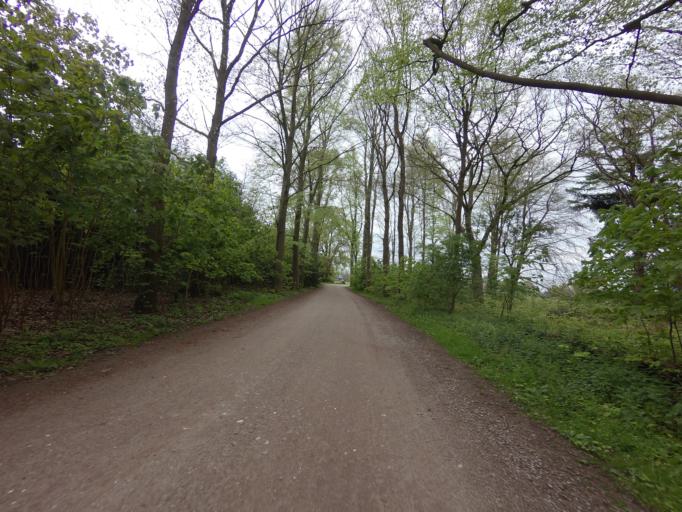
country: NL
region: Utrecht
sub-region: Gemeente De Bilt
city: De Bilt
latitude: 52.1371
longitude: 5.1752
